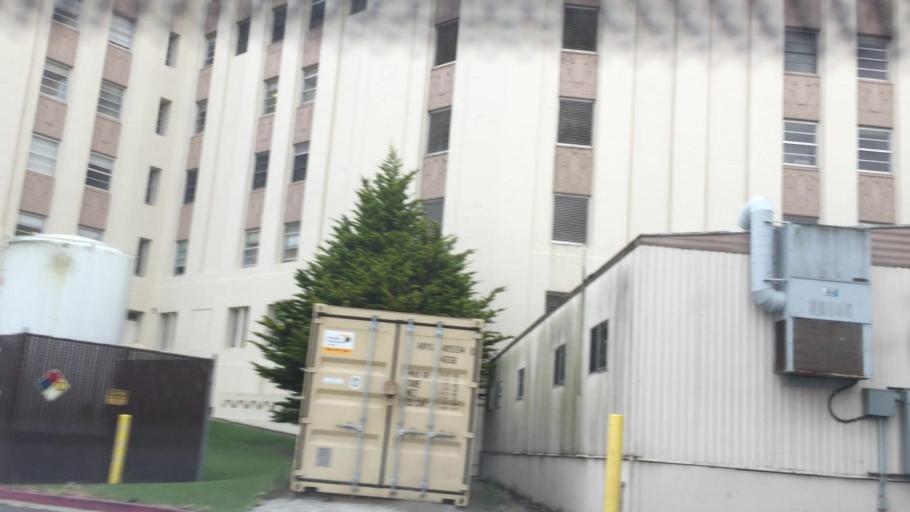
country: US
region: California
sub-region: Marin County
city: Sausalito
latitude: 37.7831
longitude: -122.5053
